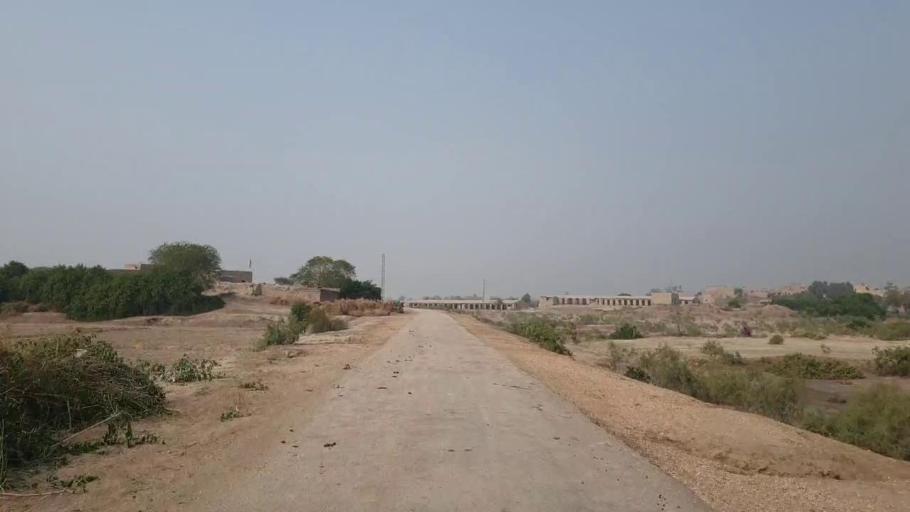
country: PK
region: Sindh
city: Bhan
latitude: 26.5039
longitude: 67.6921
